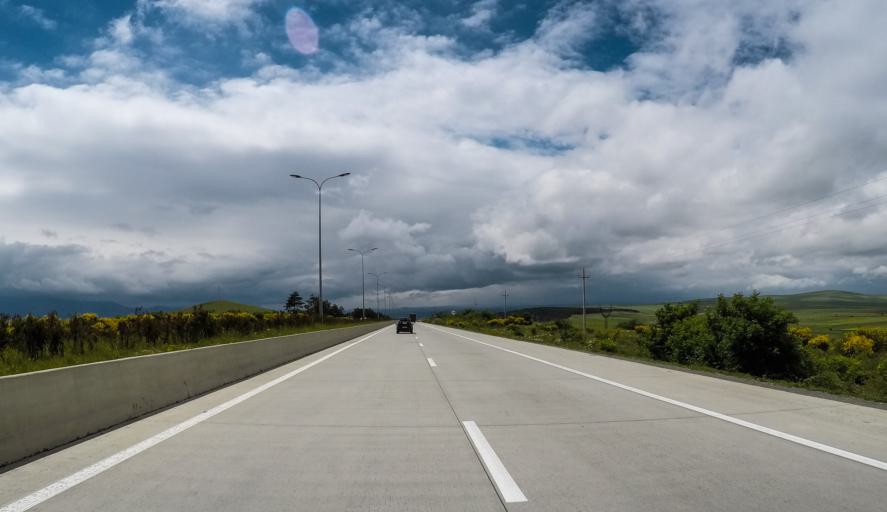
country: GE
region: Shida Kartli
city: Gori
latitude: 42.0183
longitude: 44.0199
